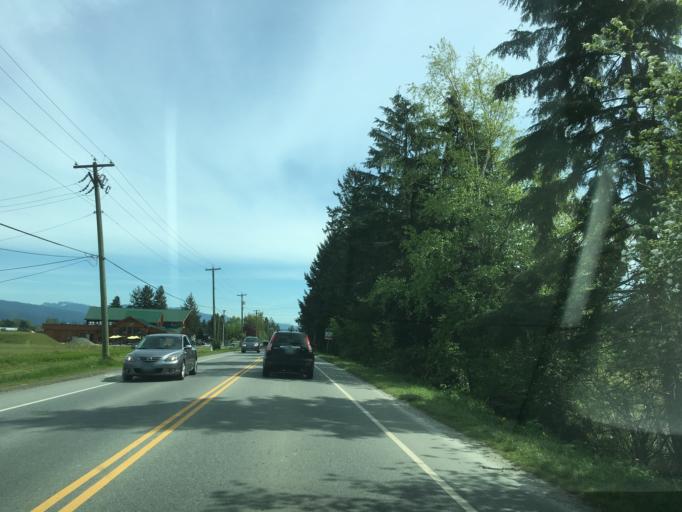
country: CA
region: British Columbia
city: Pitt Meadows
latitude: 49.2443
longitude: -122.7151
